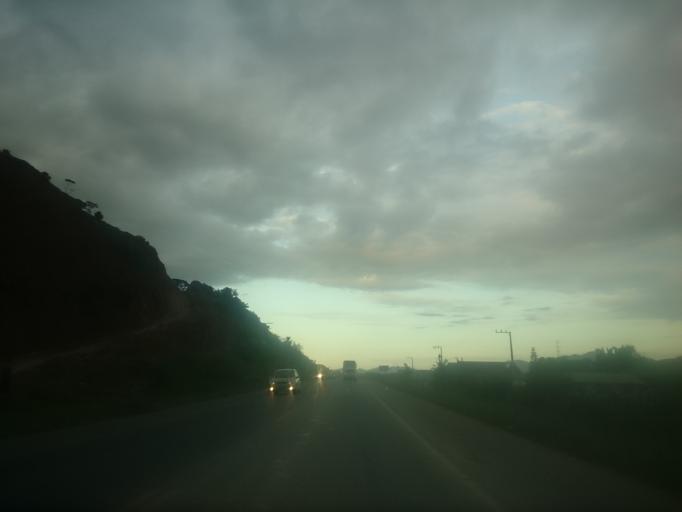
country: BR
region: Santa Catarina
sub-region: Gaspar
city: Gaspar
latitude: -26.8935
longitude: -48.9121
